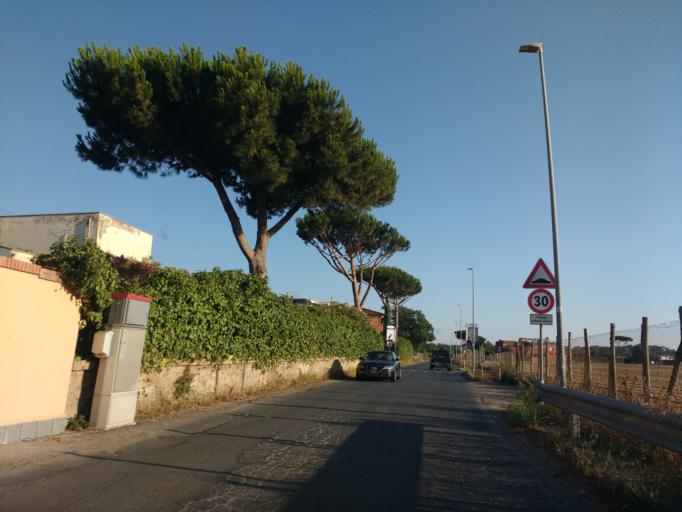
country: IT
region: Latium
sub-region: Citta metropolitana di Roma Capitale
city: Fregene
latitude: 41.8541
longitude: 12.2185
